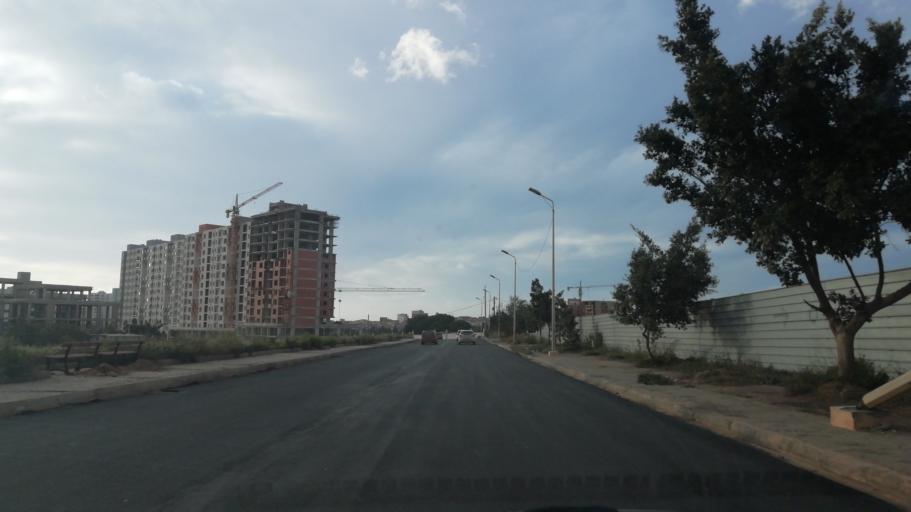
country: DZ
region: Oran
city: Bir el Djir
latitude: 35.7120
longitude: -0.5706
